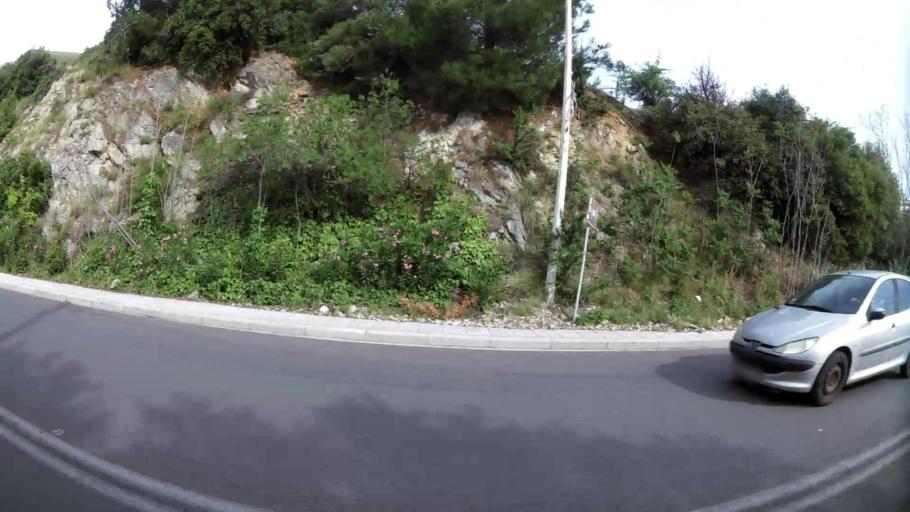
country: GR
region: Central Macedonia
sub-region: Nomos Thessalonikis
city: Panorama
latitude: 40.5838
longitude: 23.0341
